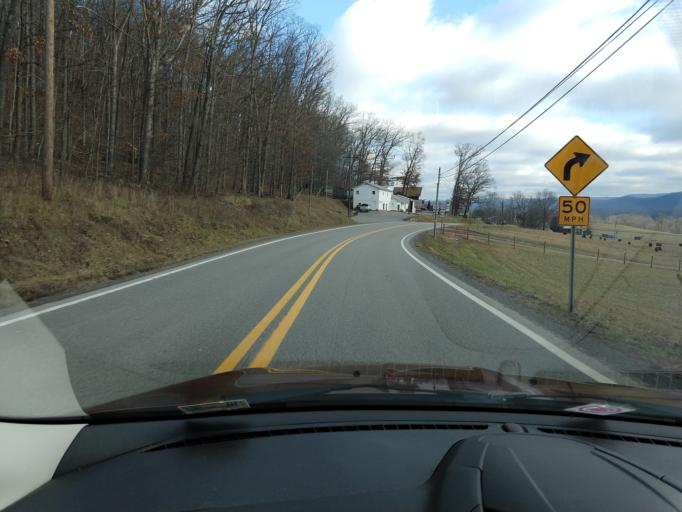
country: US
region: West Virginia
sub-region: Randolph County
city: Elkins
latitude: 38.7778
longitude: -79.9176
